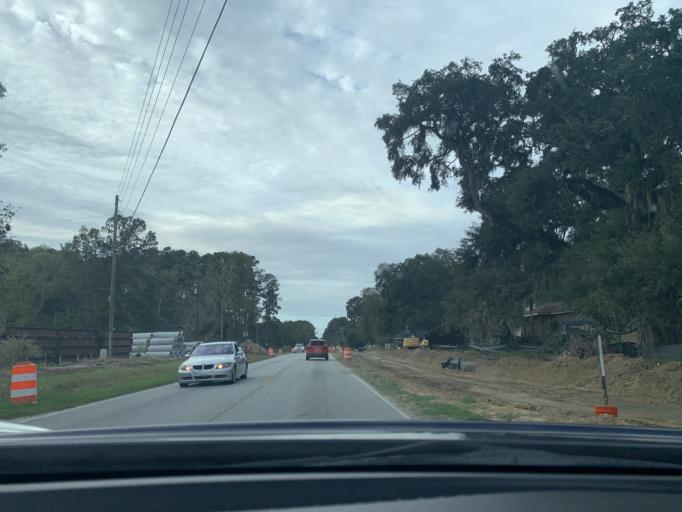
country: US
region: Georgia
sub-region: Chatham County
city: Georgetown
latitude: 32.0169
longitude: -81.2362
